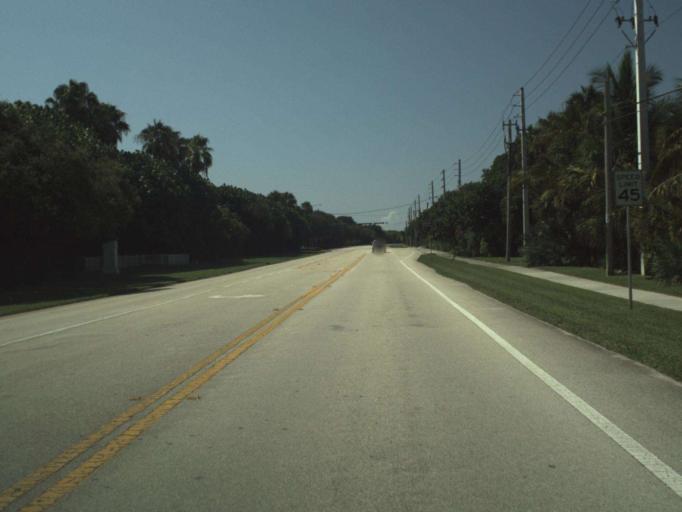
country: US
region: Florida
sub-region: Indian River County
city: Wabasso Beach
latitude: 27.7566
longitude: -80.3944
